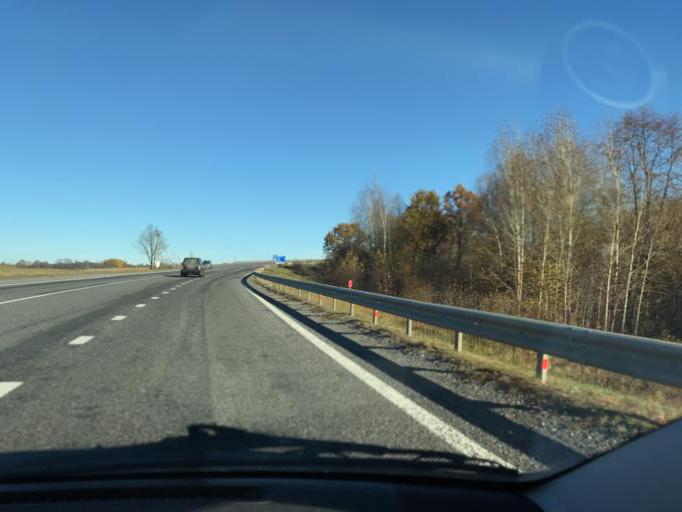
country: BY
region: Vitebsk
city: Vitebsk
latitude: 55.0977
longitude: 30.3004
